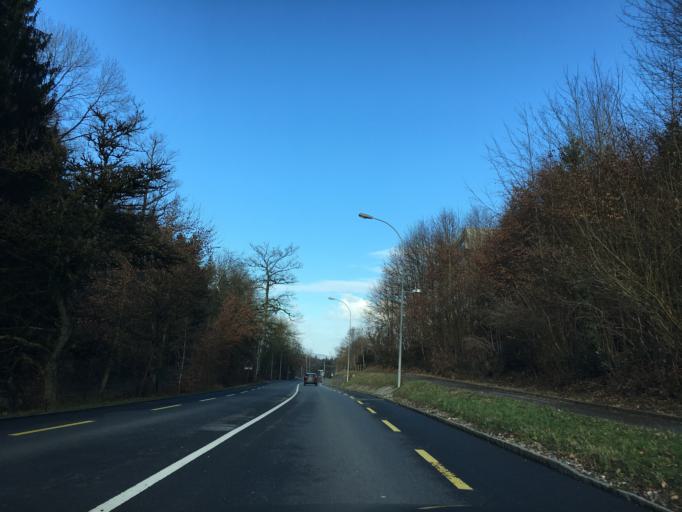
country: CH
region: Lucerne
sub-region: Lucerne-Land District
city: Ebikon
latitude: 47.0638
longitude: 8.3244
